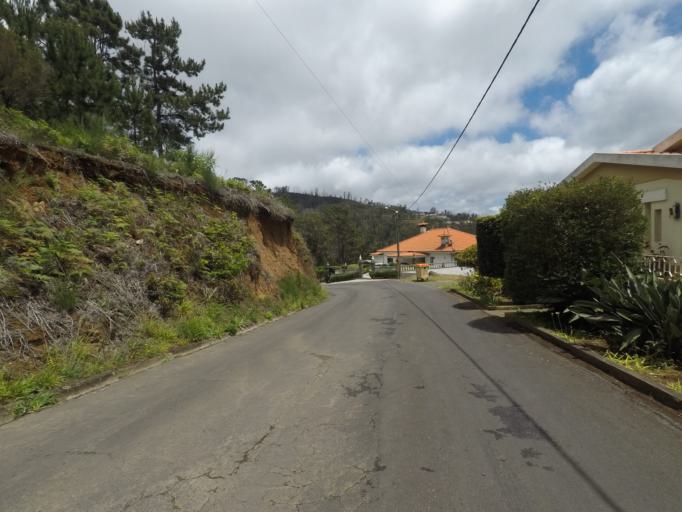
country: PT
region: Madeira
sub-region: Calheta
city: Estreito da Calheta
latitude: 32.7543
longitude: -17.1995
